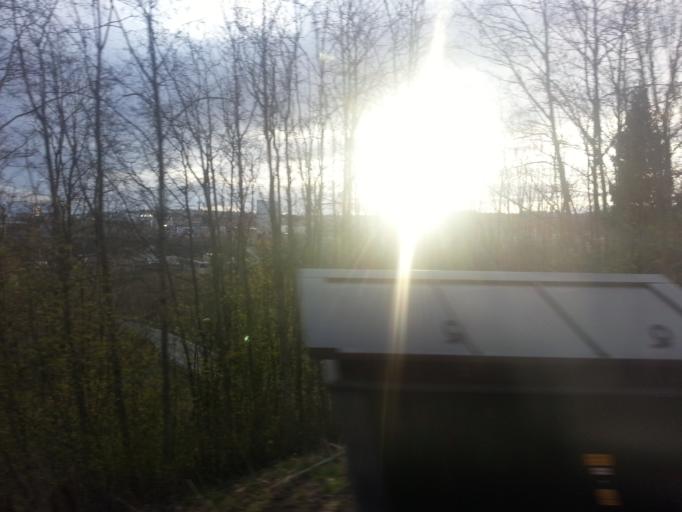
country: NO
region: Sor-Trondelag
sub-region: Trondheim
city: Trondheim
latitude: 63.4067
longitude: 10.3840
